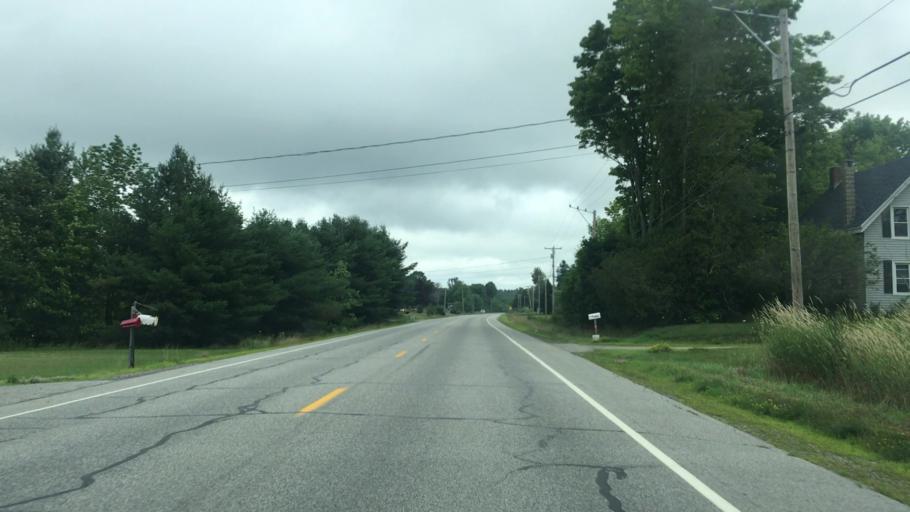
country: US
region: Maine
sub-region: Kennebec County
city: Pittston
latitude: 44.1558
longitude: -69.7446
